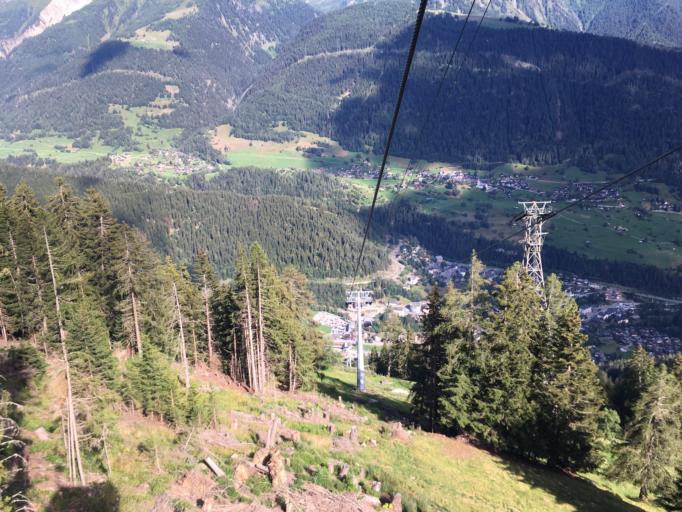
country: CH
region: Valais
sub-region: Goms District
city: Fiesch
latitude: 46.4094
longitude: 8.1199
